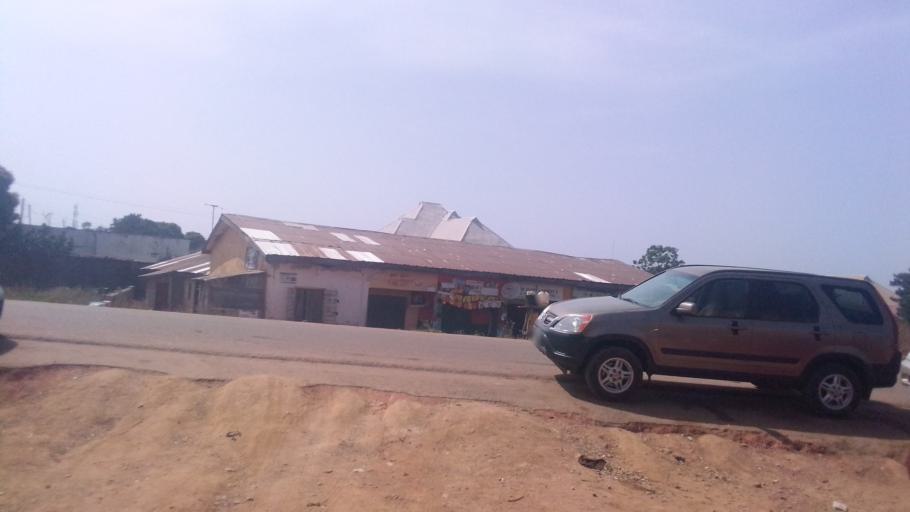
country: NG
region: Plateau
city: Jos
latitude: 9.9410
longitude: 8.8602
